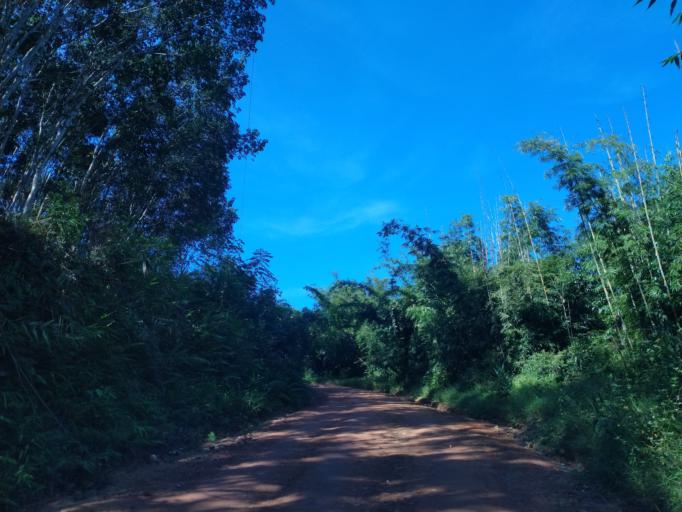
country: TH
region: Changwat Bueng Kan
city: Pak Khat
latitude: 18.6349
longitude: 103.0506
